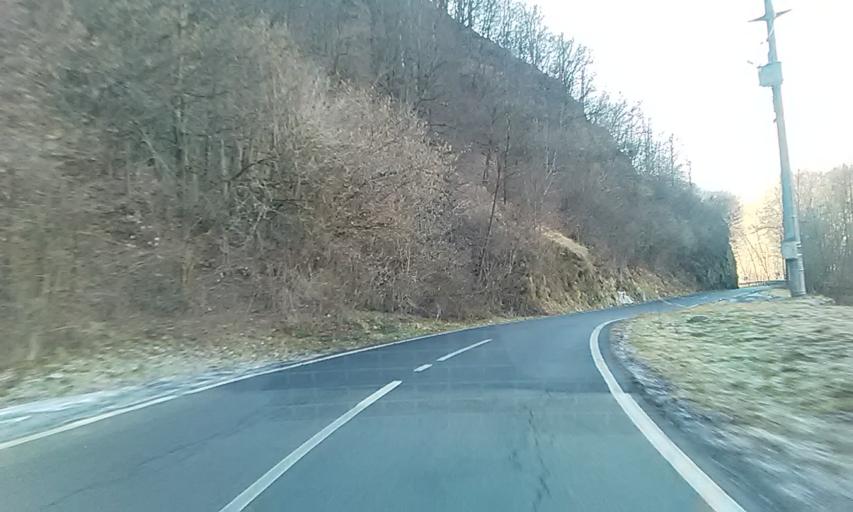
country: IT
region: Piedmont
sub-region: Provincia di Vercelli
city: Guardabosone
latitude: 45.6946
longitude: 8.2544
